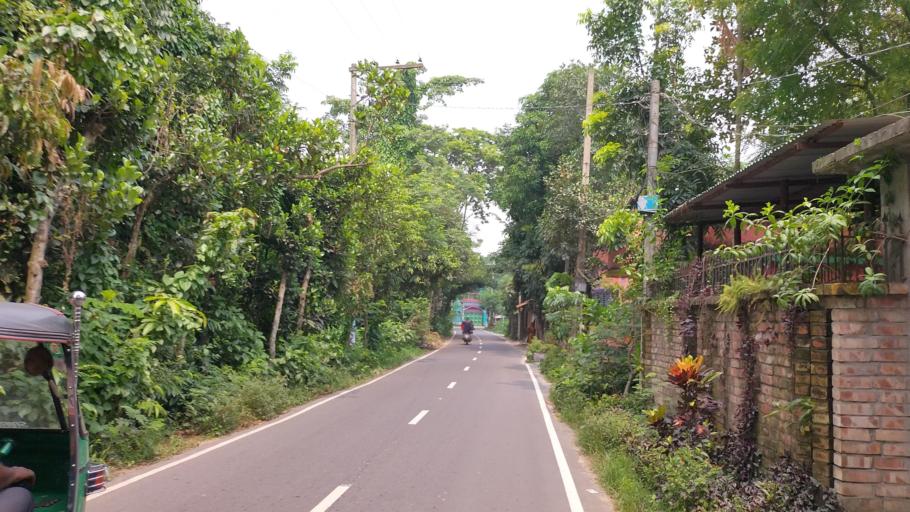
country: BD
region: Dhaka
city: Azimpur
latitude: 23.7181
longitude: 90.2778
